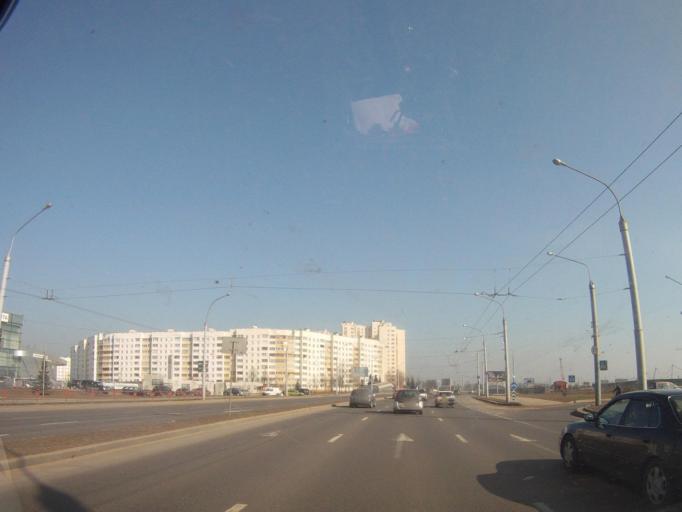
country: BY
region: Minsk
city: Minsk
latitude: 53.9270
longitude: 27.5069
